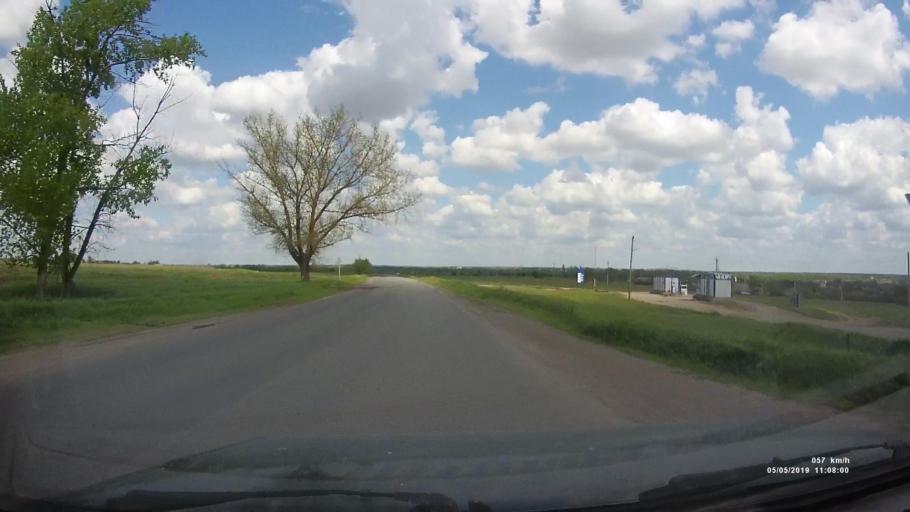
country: RU
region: Rostov
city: Ust'-Donetskiy
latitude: 47.7305
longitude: 40.9138
